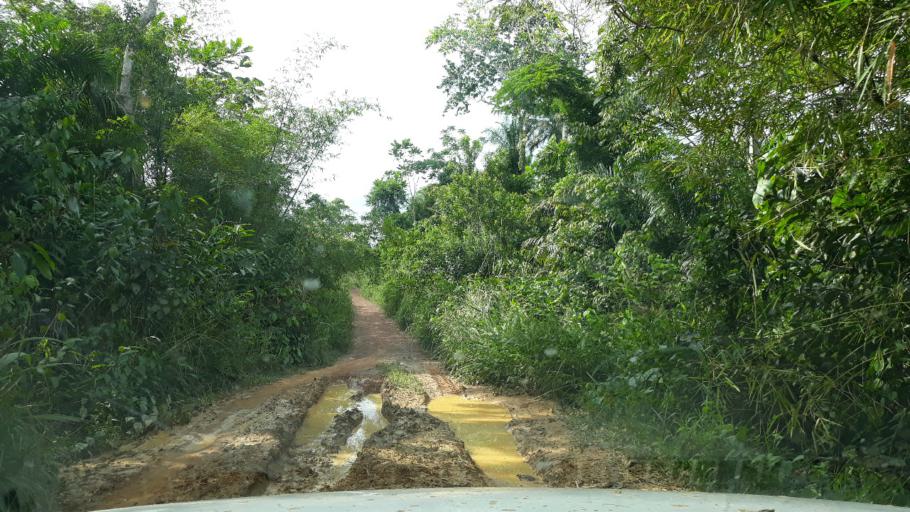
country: CD
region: Maniema
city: Kampene
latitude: -2.7610
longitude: 26.9286
